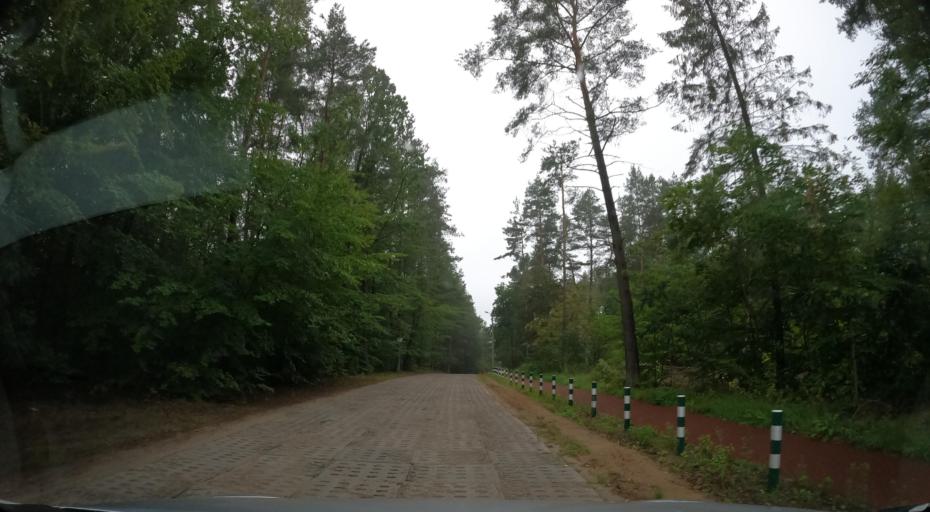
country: PL
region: Pomeranian Voivodeship
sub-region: Powiat kartuski
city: Chwaszczyno
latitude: 54.4343
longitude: 18.4180
